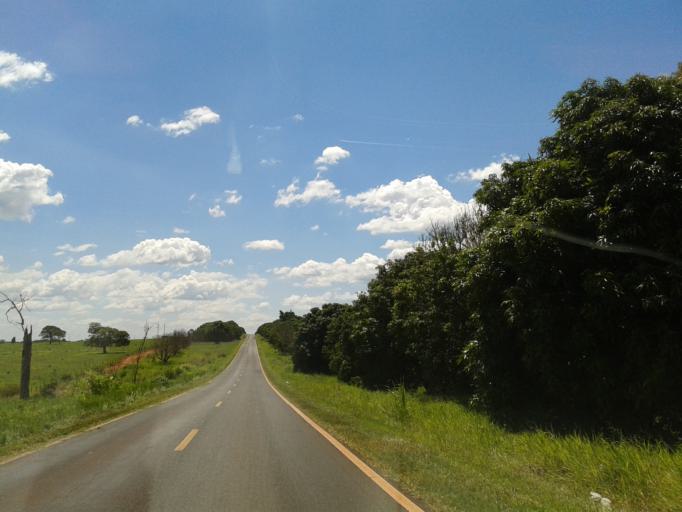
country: BR
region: Minas Gerais
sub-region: Centralina
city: Centralina
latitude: -18.7238
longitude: -49.1711
